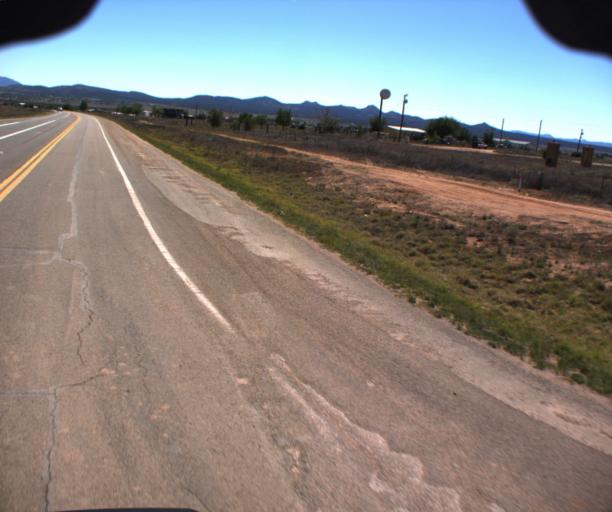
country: US
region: Arizona
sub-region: Yavapai County
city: Paulden
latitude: 34.9105
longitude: -112.4603
